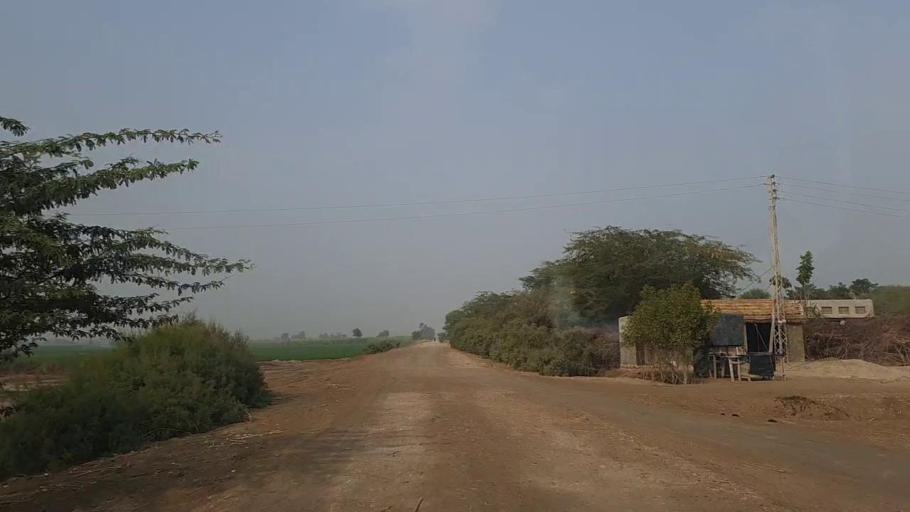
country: PK
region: Sindh
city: Sanghar
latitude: 26.1101
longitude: 68.8963
